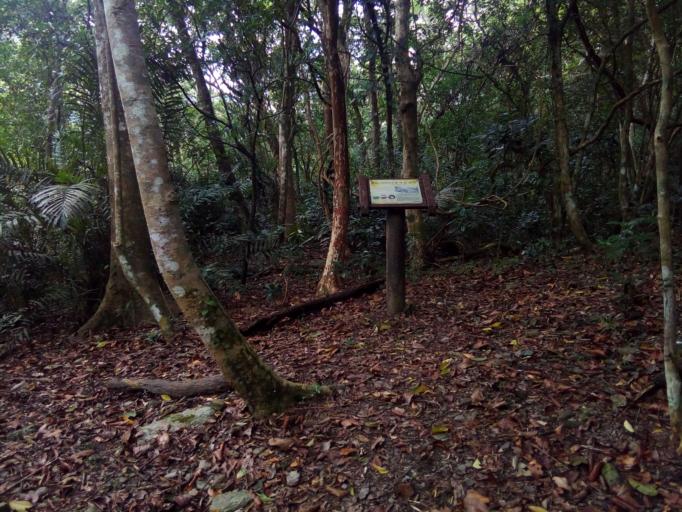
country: TW
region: Taiwan
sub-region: Taitung
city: Taitung
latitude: 23.3173
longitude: 121.2571
